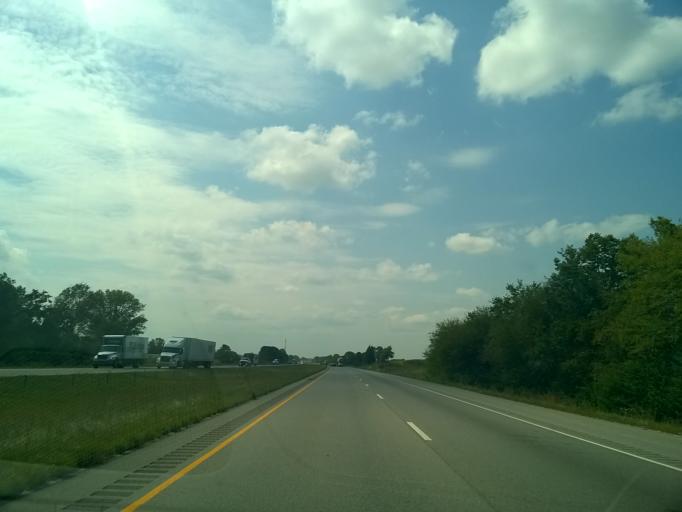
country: US
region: Indiana
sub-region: Morgan County
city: Monrovia
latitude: 39.5855
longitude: -86.5767
